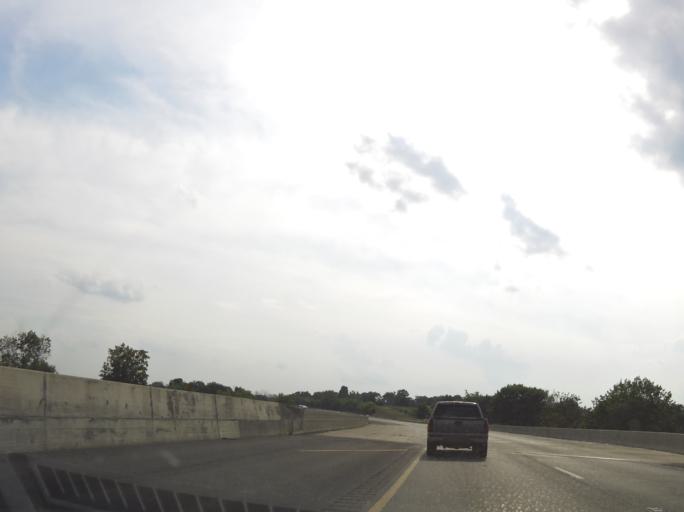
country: US
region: Maryland
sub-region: Washington County
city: Williamsport
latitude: 39.5803
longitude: -77.8751
